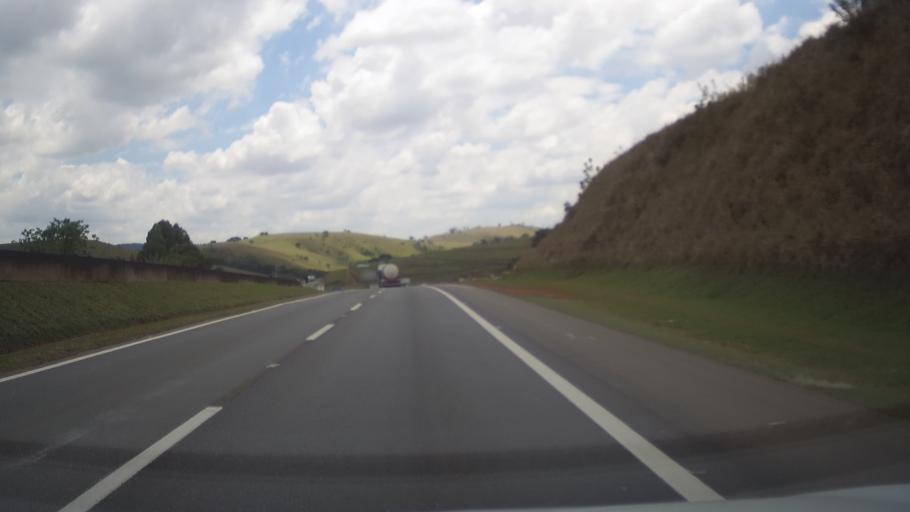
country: BR
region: Minas Gerais
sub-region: Campanha
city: Campanha
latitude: -21.7149
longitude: -45.3766
